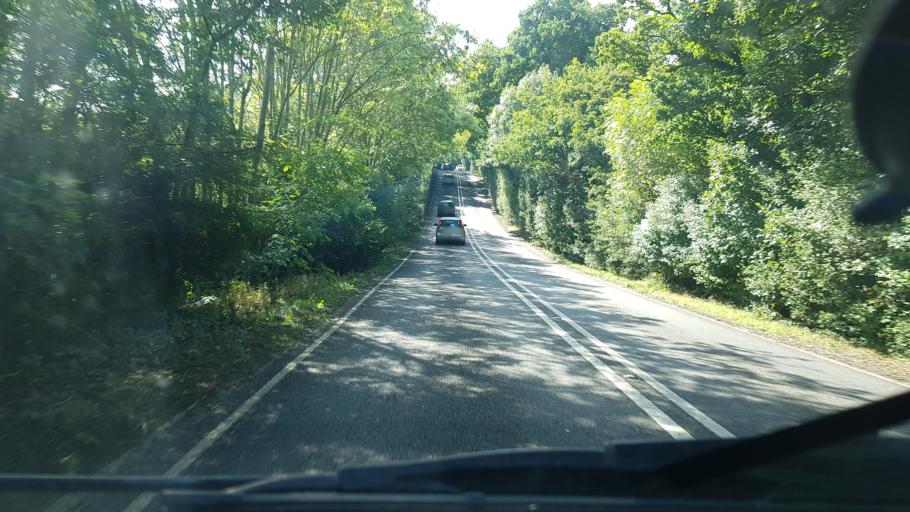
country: GB
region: England
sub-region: West Sussex
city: Rudgwick
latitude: 51.0857
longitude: -0.4454
